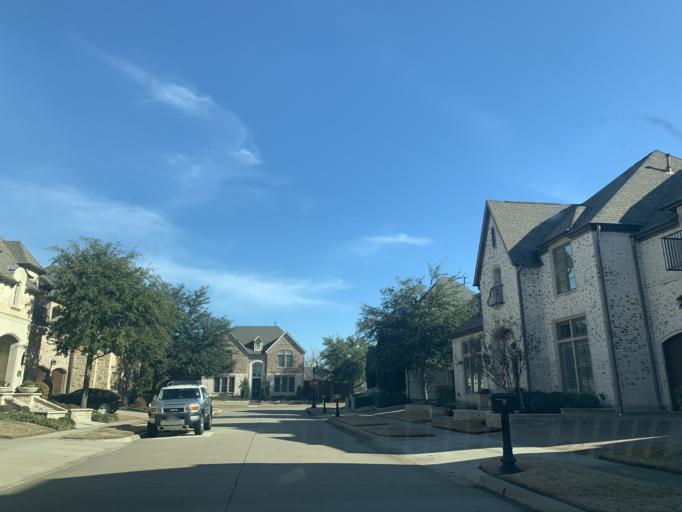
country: US
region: Texas
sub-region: Denton County
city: The Colony
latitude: 33.0582
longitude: -96.8200
